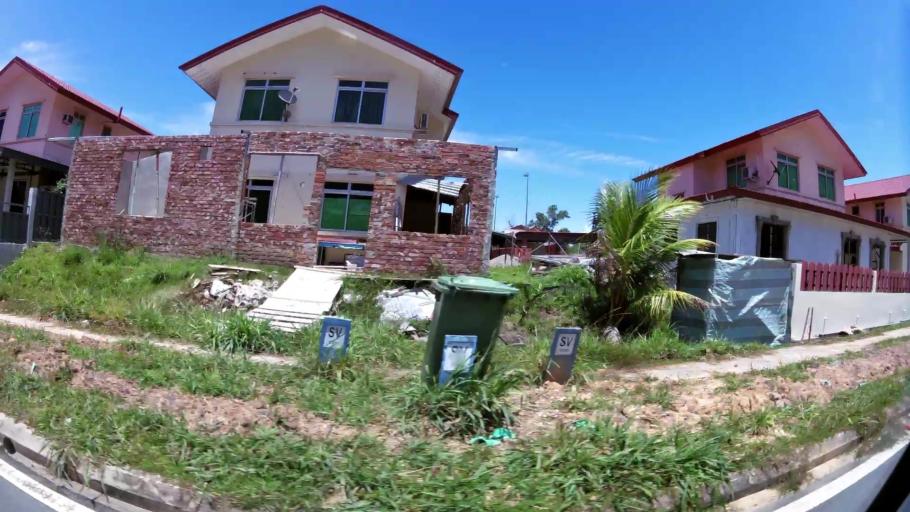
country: BN
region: Brunei and Muara
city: Bandar Seri Begawan
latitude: 5.0160
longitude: 115.0301
